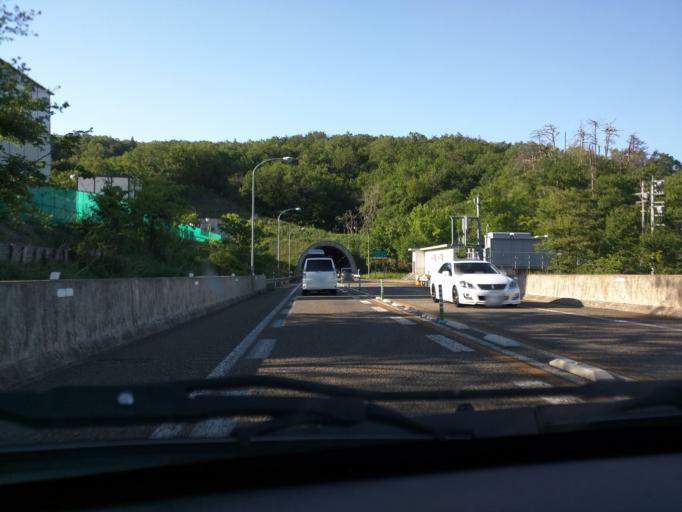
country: JP
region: Niigata
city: Arai
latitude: 37.0422
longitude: 138.2322
